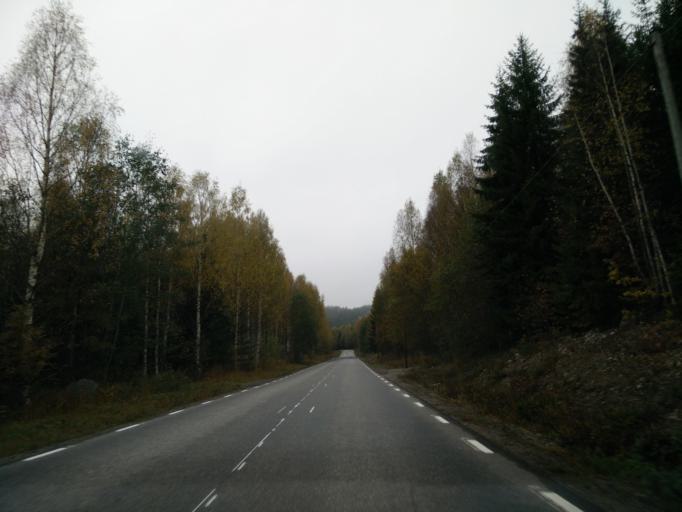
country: SE
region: Vaesternorrland
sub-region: Sundsvalls Kommun
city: Nolby
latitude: 62.3045
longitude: 17.2807
